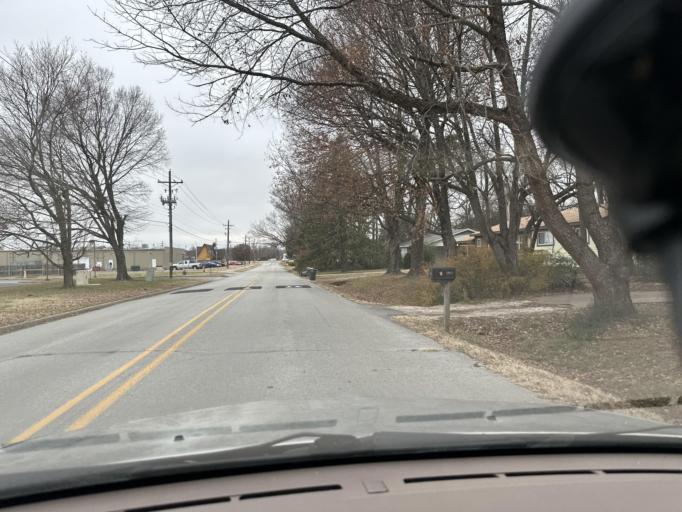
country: US
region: Arkansas
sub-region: Washington County
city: Johnson
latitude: 36.1097
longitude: -94.1421
